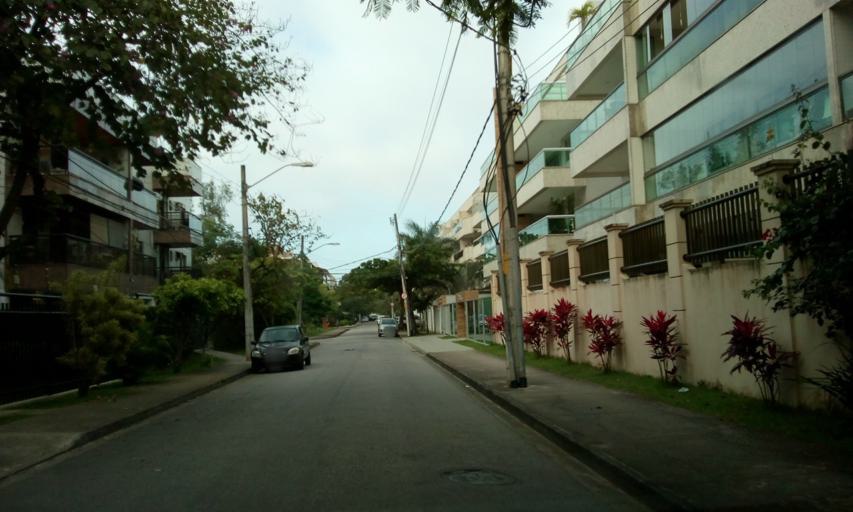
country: BR
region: Rio de Janeiro
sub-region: Nilopolis
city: Nilopolis
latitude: -23.0149
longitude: -43.4509
